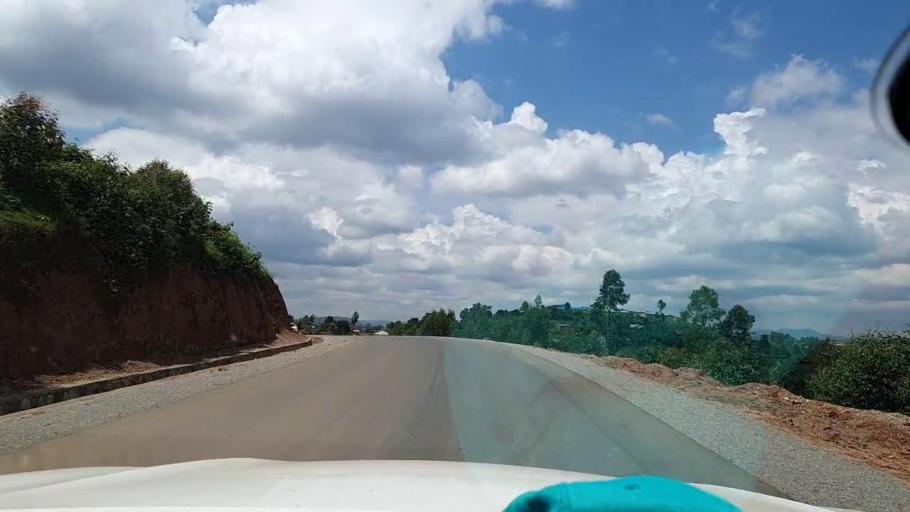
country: RW
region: Southern Province
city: Nzega
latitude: -2.6441
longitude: 29.5728
